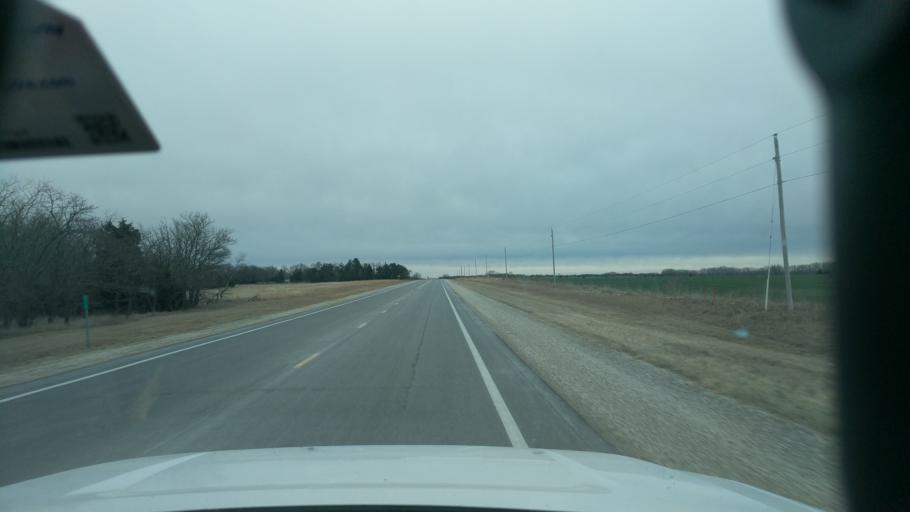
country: US
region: Kansas
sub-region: Marion County
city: Marion
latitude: 38.4836
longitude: -96.9578
